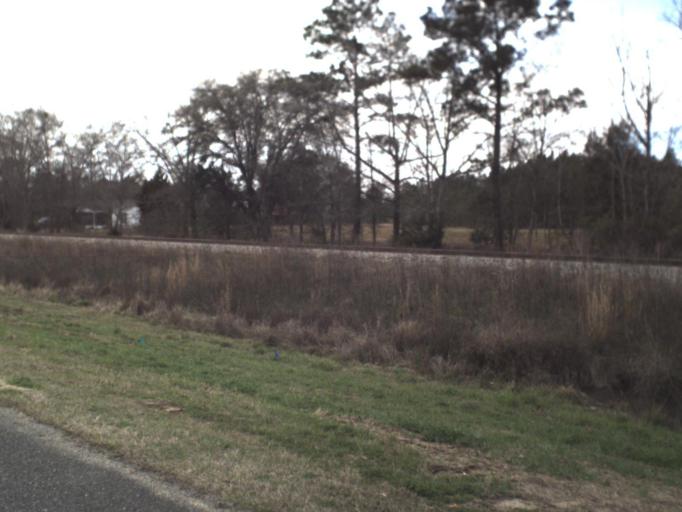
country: US
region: Florida
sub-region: Washington County
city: Chipley
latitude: 30.7480
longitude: -85.3842
